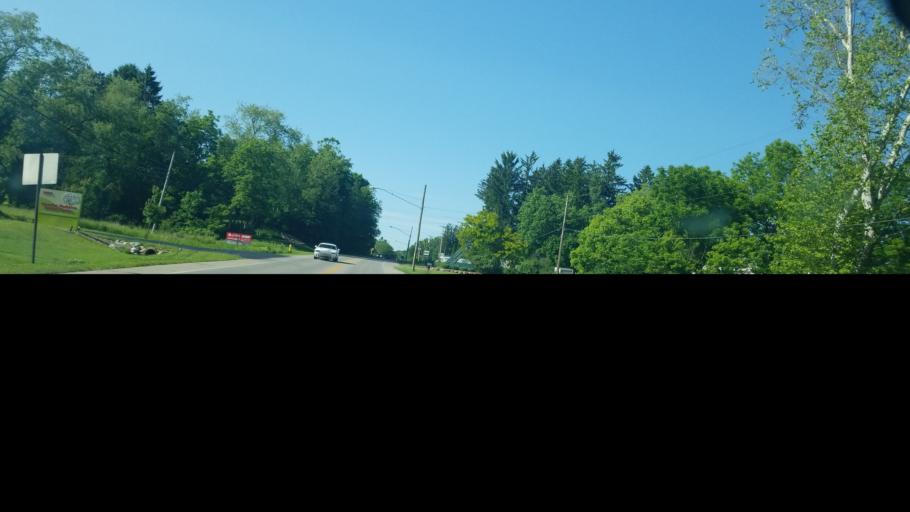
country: US
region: Ohio
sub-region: Wayne County
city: Wooster
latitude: 40.8432
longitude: -81.9291
